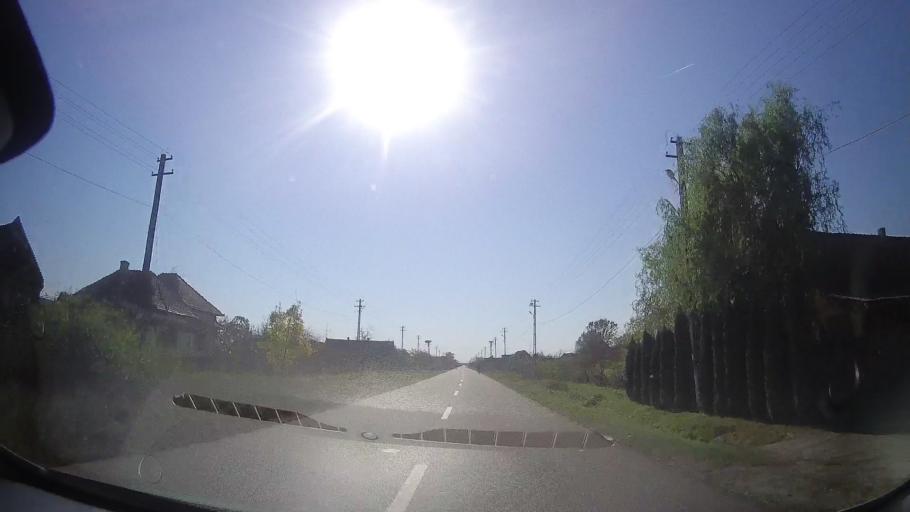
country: RO
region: Timis
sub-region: Comuna Ghizela
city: Ghizela
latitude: 45.7982
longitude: 21.7262
